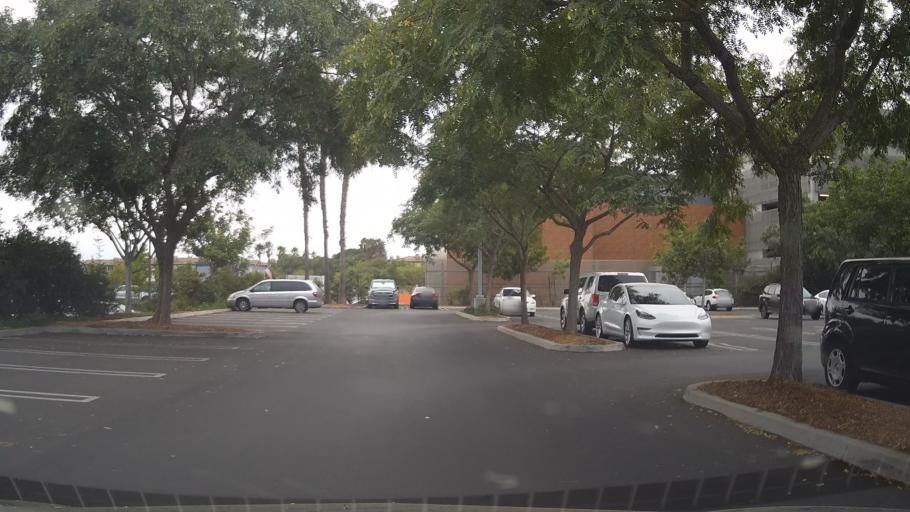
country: US
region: California
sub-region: San Diego County
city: San Diego
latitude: 32.8250
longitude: -117.1327
